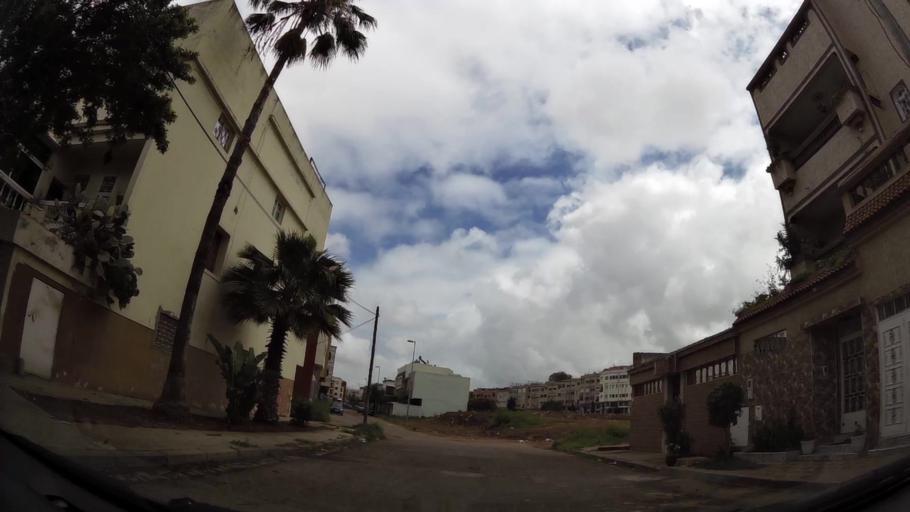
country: MA
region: Grand Casablanca
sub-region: Casablanca
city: Casablanca
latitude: 33.5340
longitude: -7.5995
